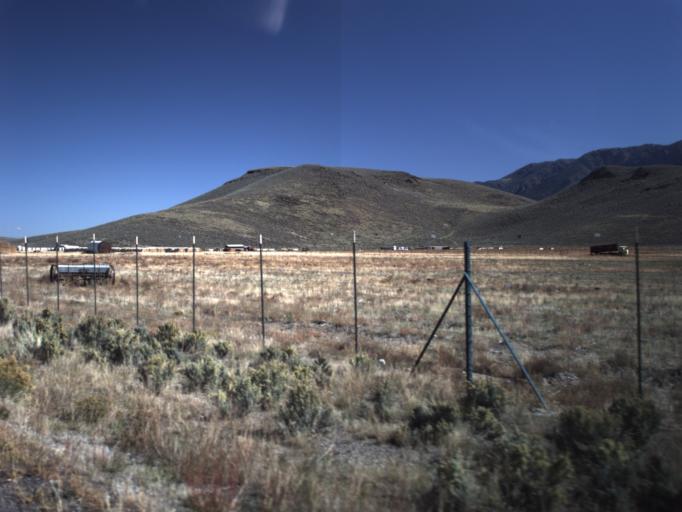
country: US
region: Utah
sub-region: Piute County
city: Junction
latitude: 38.2710
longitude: -111.9865
